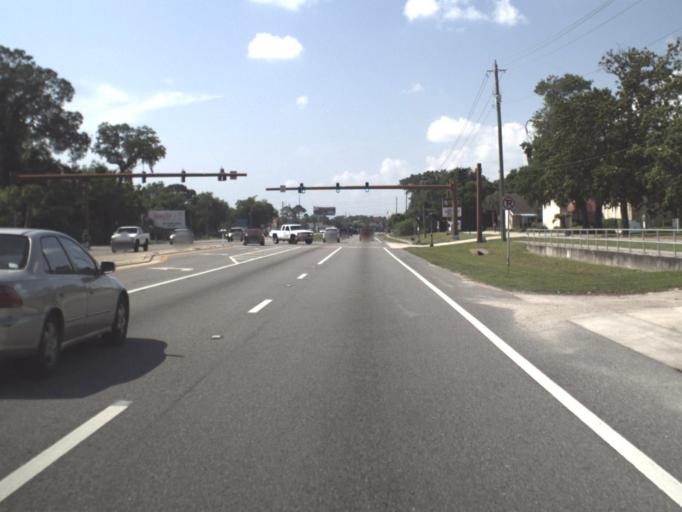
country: US
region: Florida
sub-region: Saint Johns County
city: Saint Augustine
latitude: 29.8763
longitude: -81.3242
